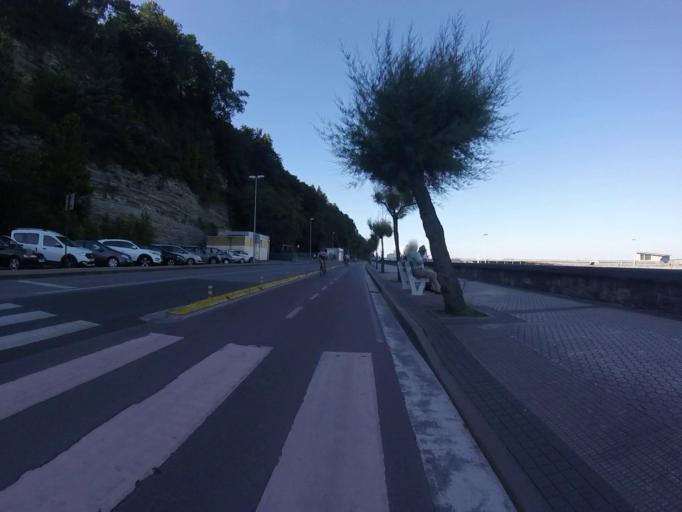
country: ES
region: Basque Country
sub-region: Provincia de Guipuzcoa
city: Fuenterrabia
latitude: 43.3847
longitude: -1.7948
